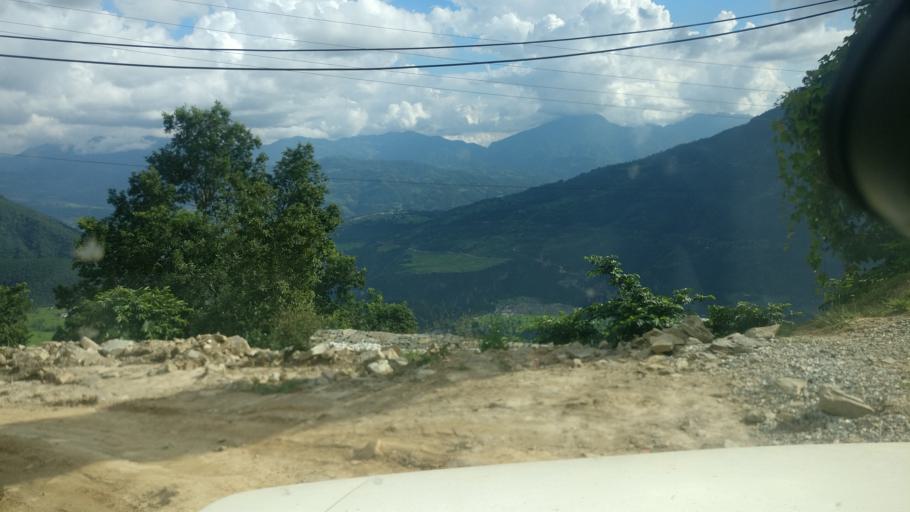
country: NP
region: Western Region
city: Baglung
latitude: 28.2656
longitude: 83.6447
